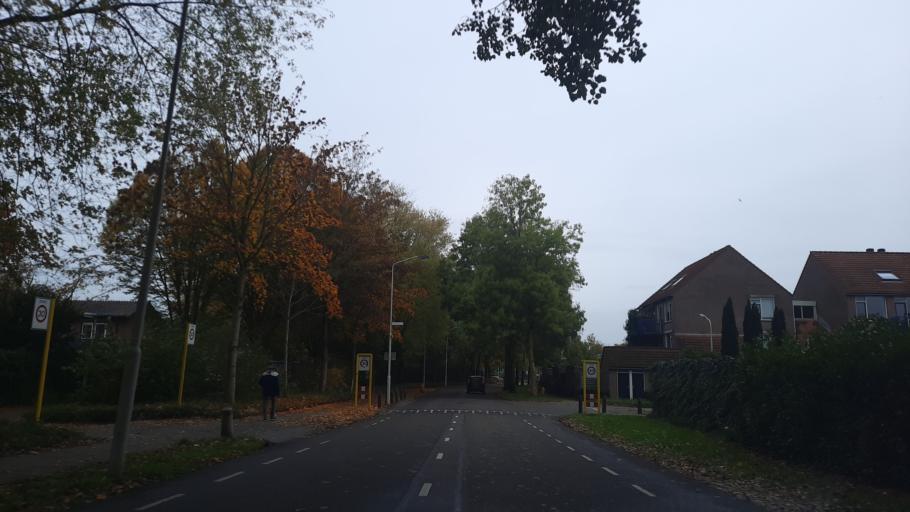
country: NL
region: South Holland
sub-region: Gemeente Gorinchem
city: Gorinchem
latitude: 51.8296
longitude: 4.9862
